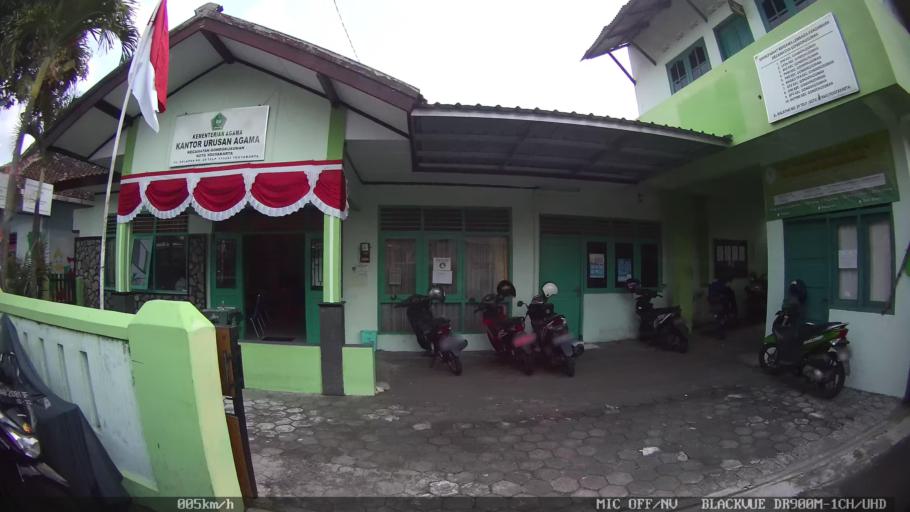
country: ID
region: Daerah Istimewa Yogyakarta
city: Yogyakarta
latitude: -7.7837
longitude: 110.3828
